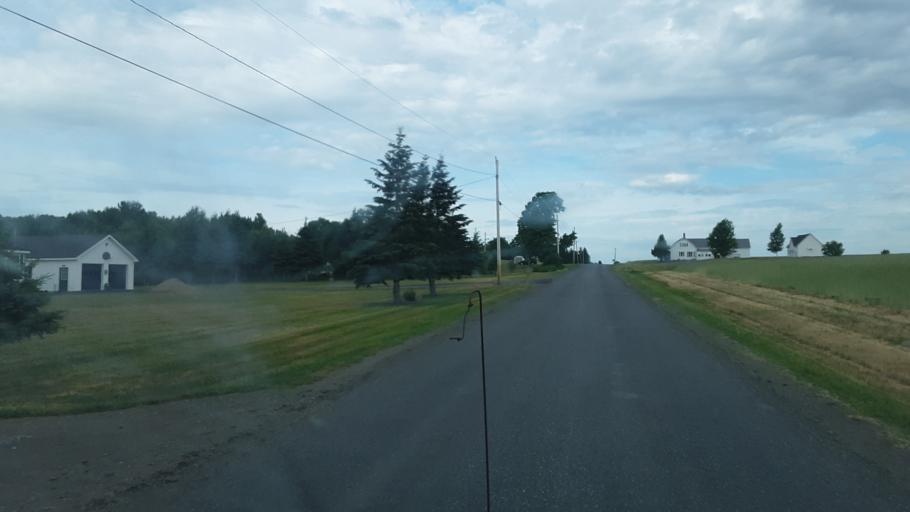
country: US
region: Maine
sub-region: Aroostook County
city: Caribou
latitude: 46.8113
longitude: -68.0105
